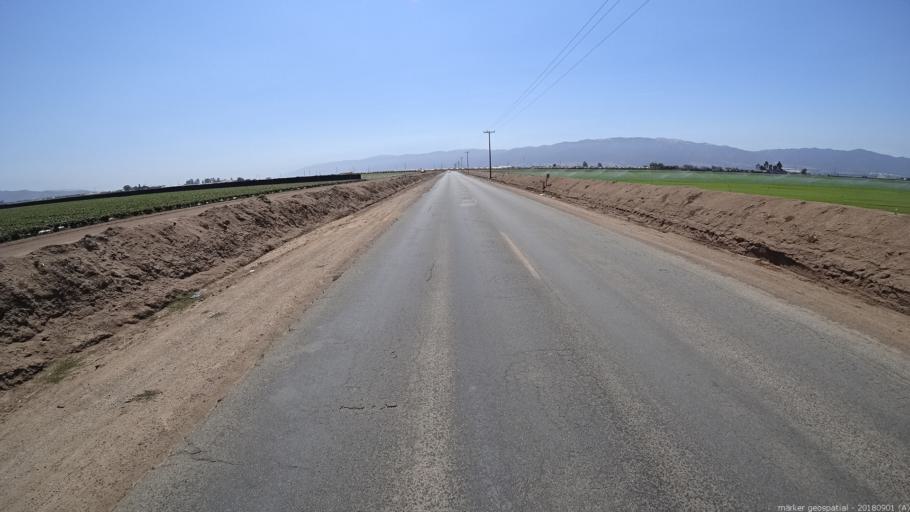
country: US
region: California
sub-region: Monterey County
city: Chualar
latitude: 36.6371
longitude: -121.5426
